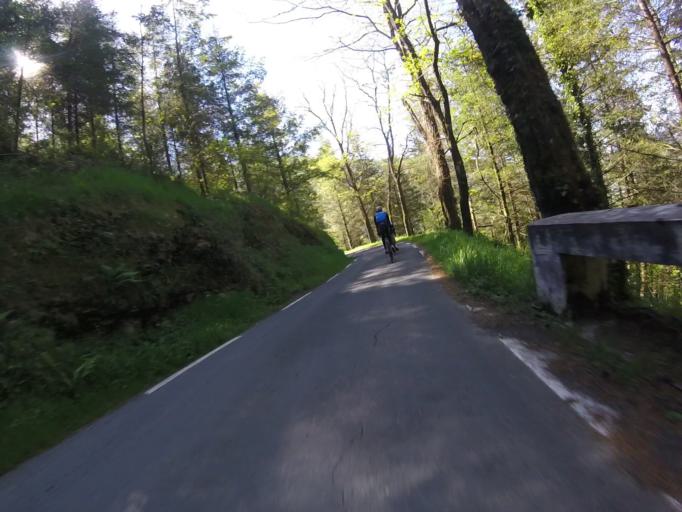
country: ES
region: Basque Country
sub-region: Provincia de Guipuzcoa
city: Errezil
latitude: 43.1907
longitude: -2.1940
